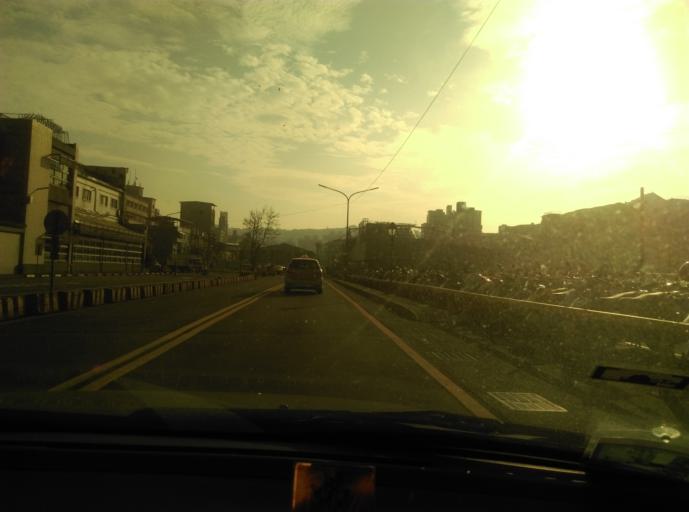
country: TW
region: Taiwan
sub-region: Keelung
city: Keelung
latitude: 25.1352
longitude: 121.7410
